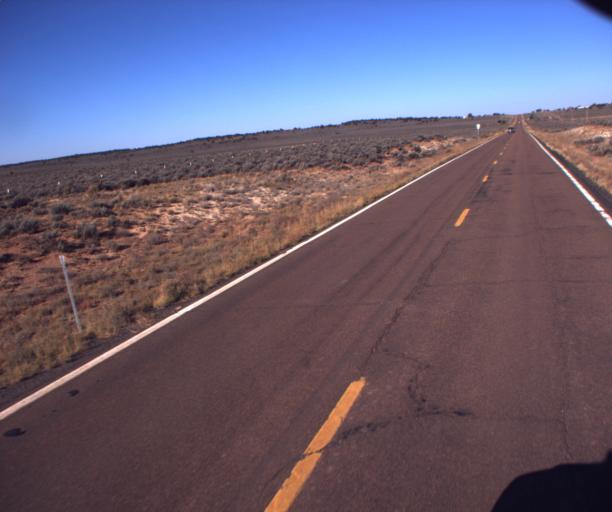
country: US
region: Arizona
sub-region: Apache County
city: Ganado
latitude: 35.7535
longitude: -109.9476
